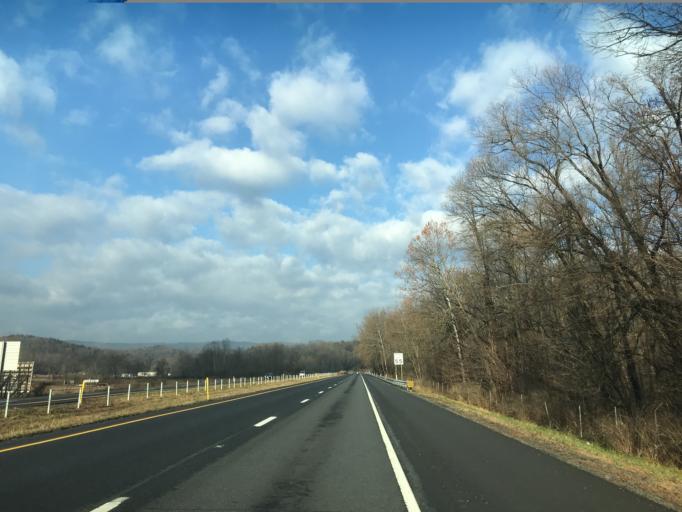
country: US
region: Maryland
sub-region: Washington County
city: Hancock
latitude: 39.7600
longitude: -78.1930
